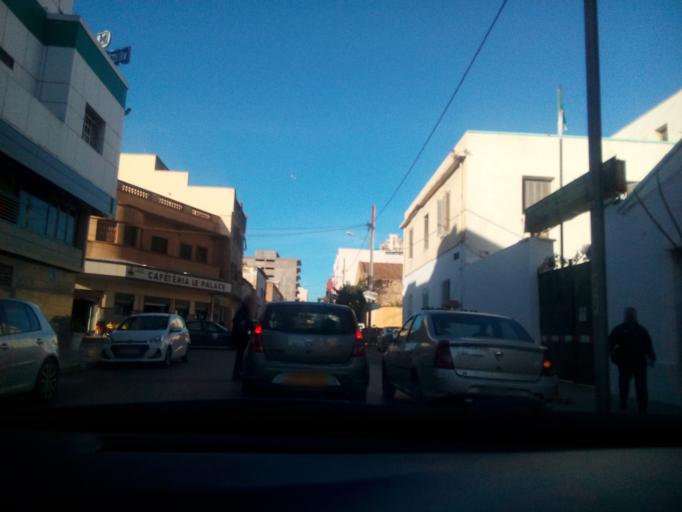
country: DZ
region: Oran
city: Oran
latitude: 35.6865
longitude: -0.6530
